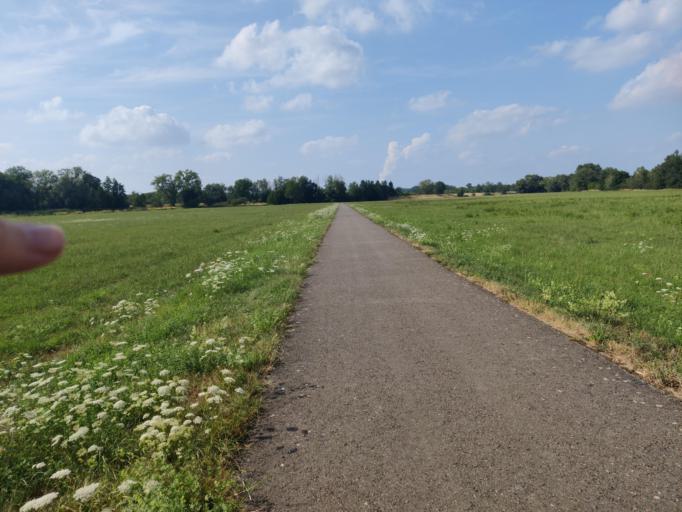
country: DE
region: Thuringia
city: Haselbach
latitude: 51.0634
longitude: 12.4460
